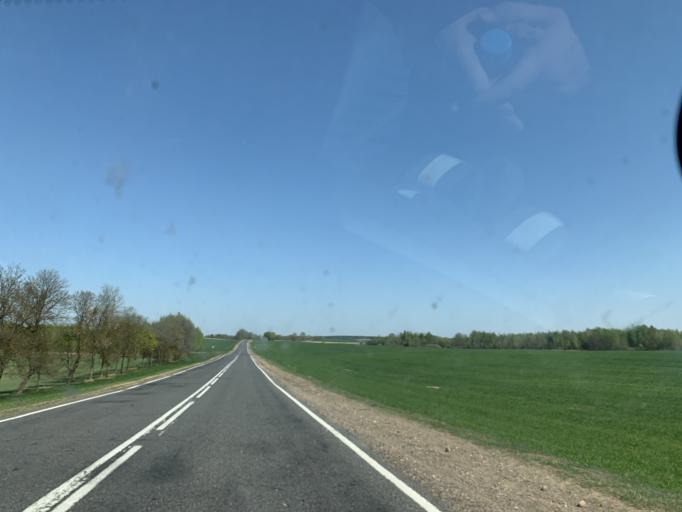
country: BY
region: Minsk
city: Nyasvizh
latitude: 53.2441
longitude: 26.8685
